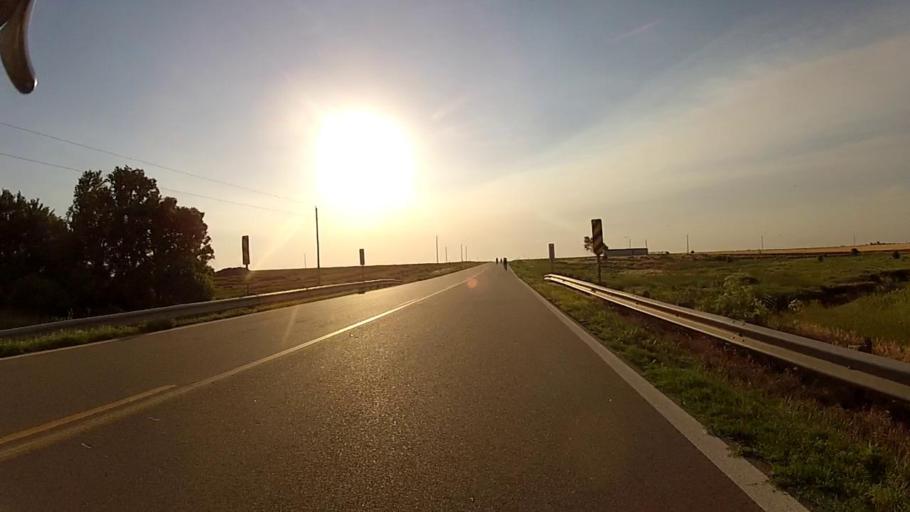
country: US
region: Kansas
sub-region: Harper County
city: Anthony
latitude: 37.1544
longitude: -97.8236
